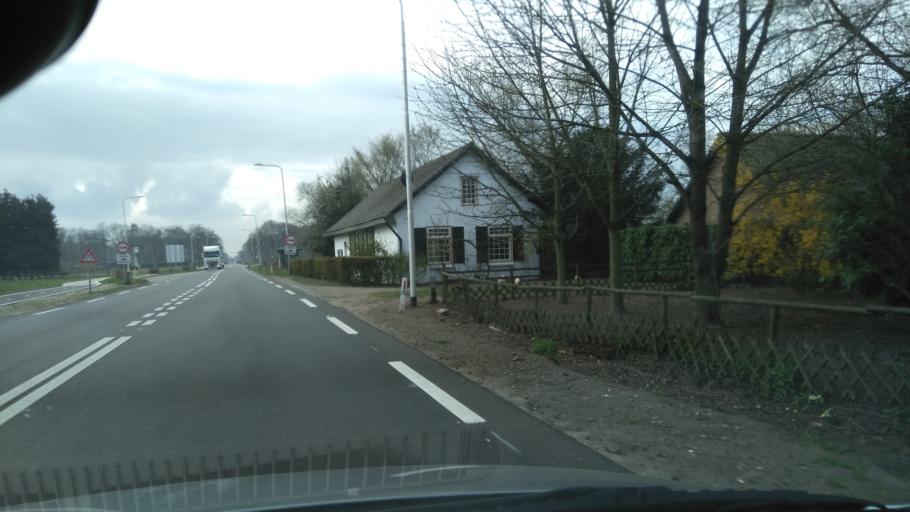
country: NL
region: North Brabant
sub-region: Gemeente Baarle-Nassau
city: Baarle-Nassau
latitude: 51.4280
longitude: 4.9330
